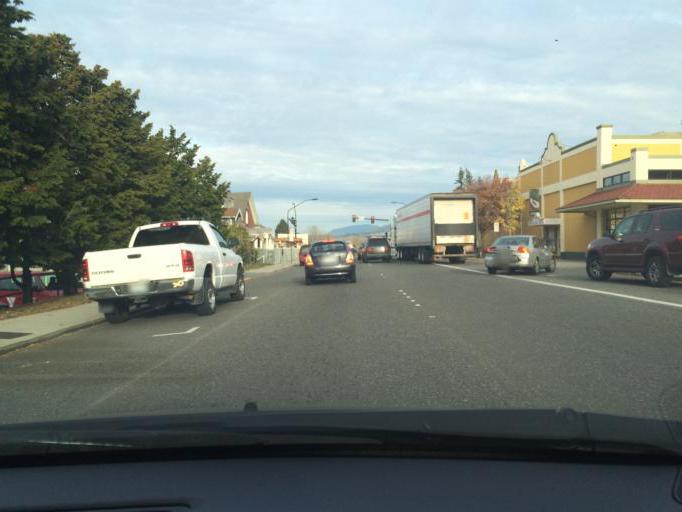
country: US
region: Washington
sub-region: Whatcom County
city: Bellingham
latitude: 48.7471
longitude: -122.4770
